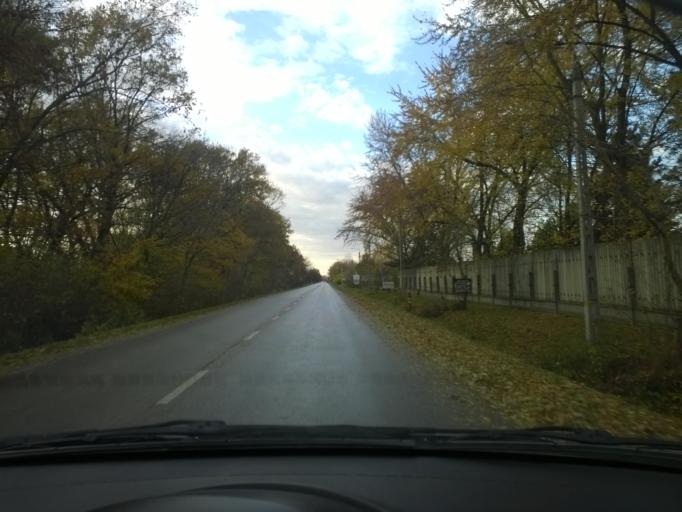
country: HU
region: Bacs-Kiskun
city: Kalocsa
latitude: 46.5165
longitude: 18.9981
